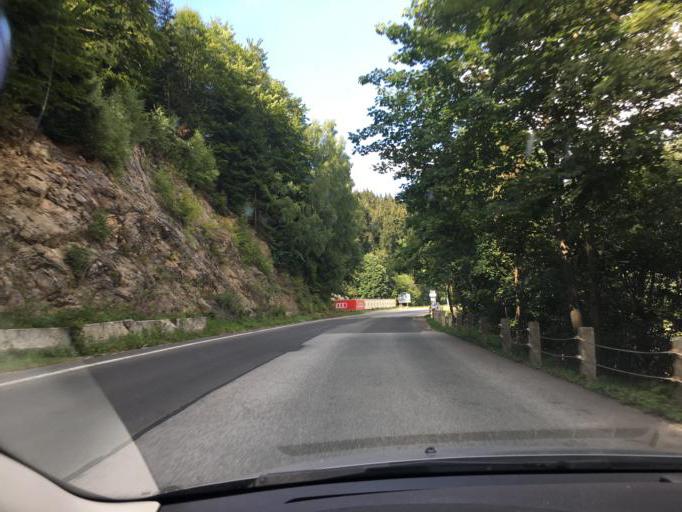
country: CZ
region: Kralovehradecky
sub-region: Okres Trutnov
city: Spindleruv Mlyn
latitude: 50.7219
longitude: 15.5887
